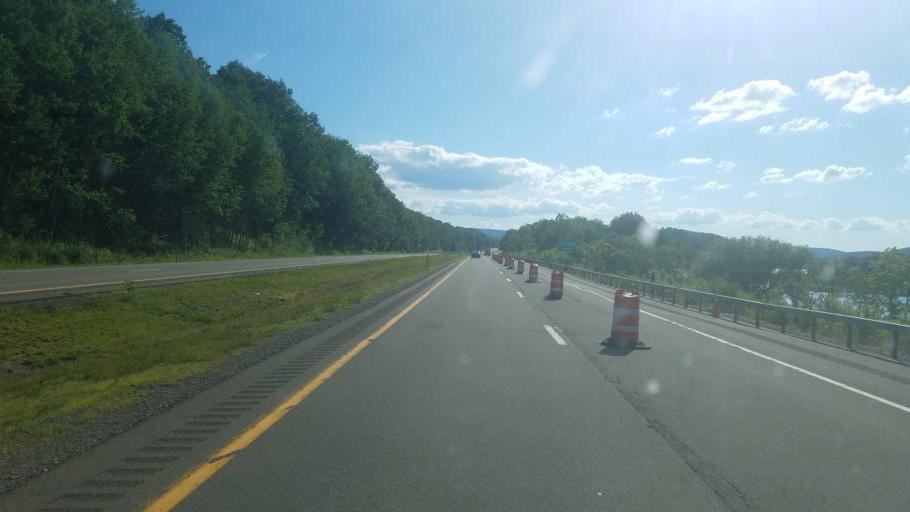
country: US
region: New York
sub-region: Cattaraugus County
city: Salamanca
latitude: 42.1036
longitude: -78.8278
